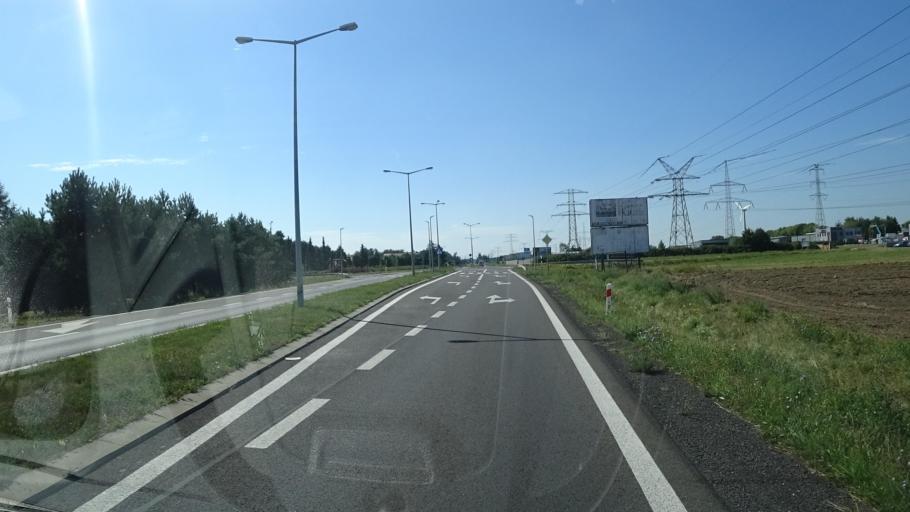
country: PL
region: Greater Poland Voivodeship
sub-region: Powiat koninski
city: Slesin
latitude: 52.3621
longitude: 18.2959
